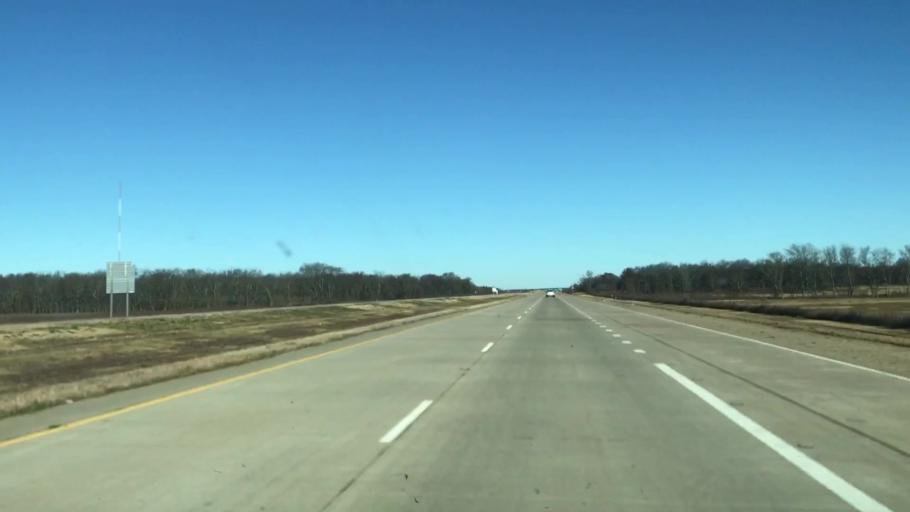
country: US
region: Louisiana
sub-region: Caddo Parish
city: Blanchard
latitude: 32.6801
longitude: -93.8522
